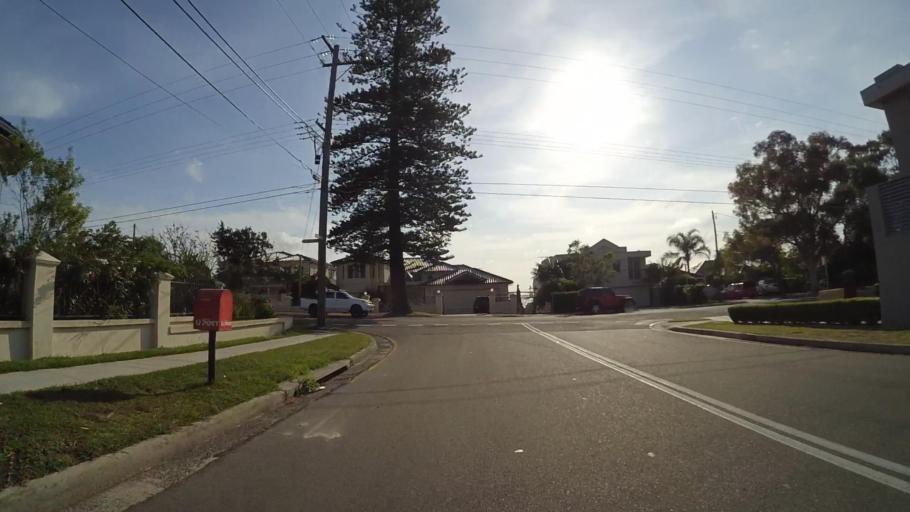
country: AU
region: New South Wales
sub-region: Kogarah
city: Blakehurst
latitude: -34.0111
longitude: 151.1138
